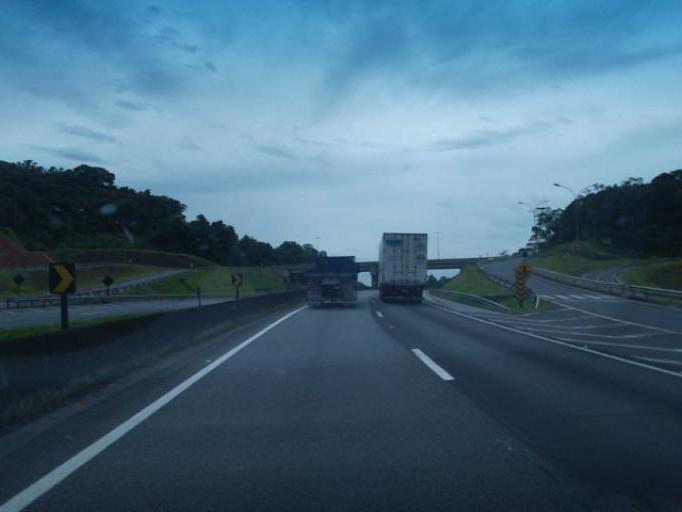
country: BR
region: Sao Paulo
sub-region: Juquia
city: Juquia
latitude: -24.3559
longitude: -47.6667
